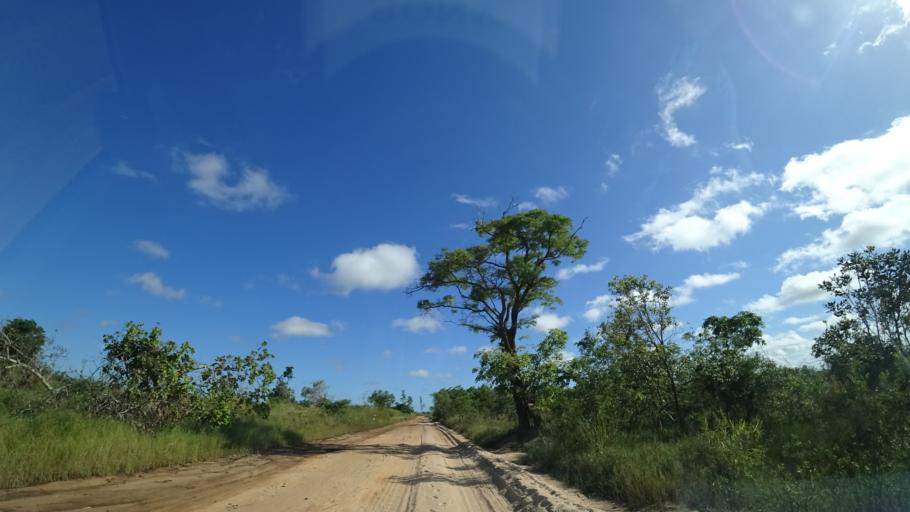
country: MZ
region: Sofala
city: Dondo
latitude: -19.4321
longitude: 34.7108
